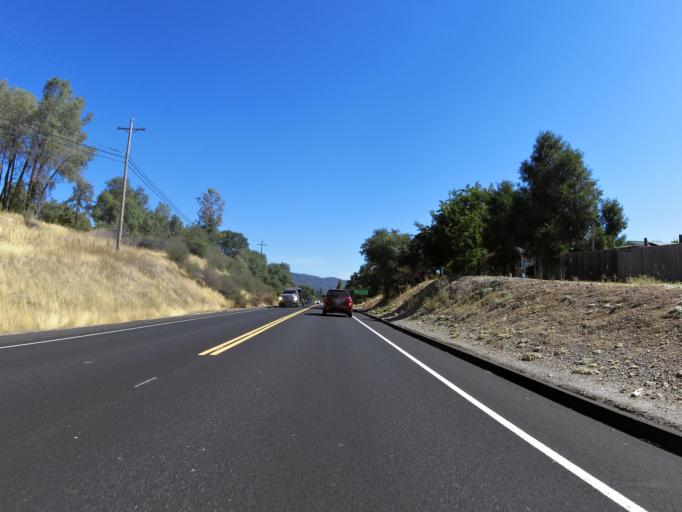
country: US
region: California
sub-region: Calaveras County
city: Murphys
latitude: 38.1099
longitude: -120.4601
